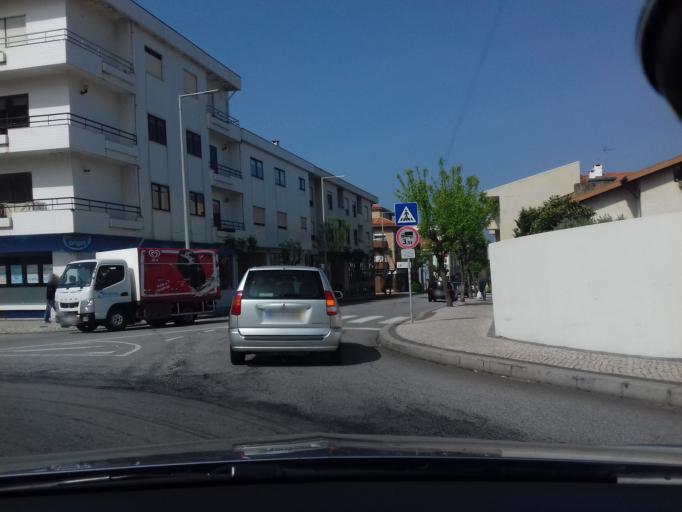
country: PT
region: Aveiro
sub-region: Espinho
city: Espinho
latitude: 41.0085
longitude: -8.6343
